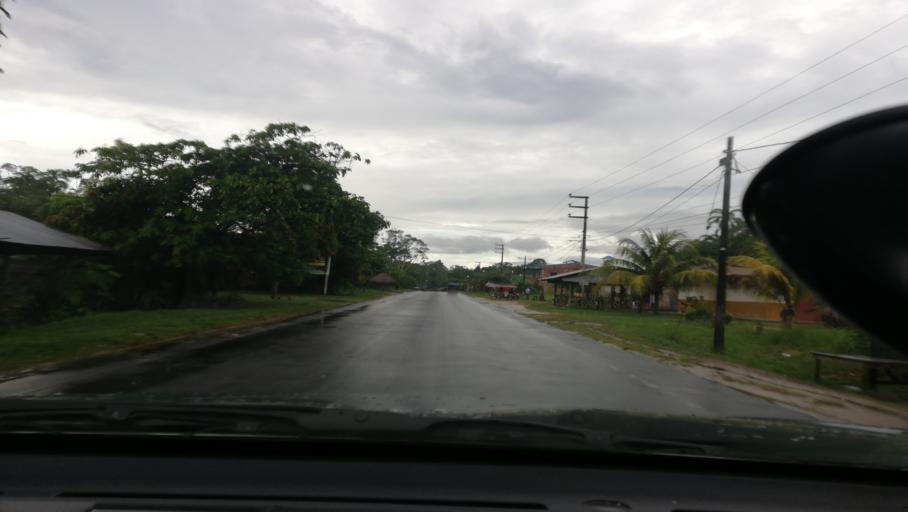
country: PE
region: Loreto
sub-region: Provincia de Maynas
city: Iquitos
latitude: -3.8889
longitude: -73.3513
